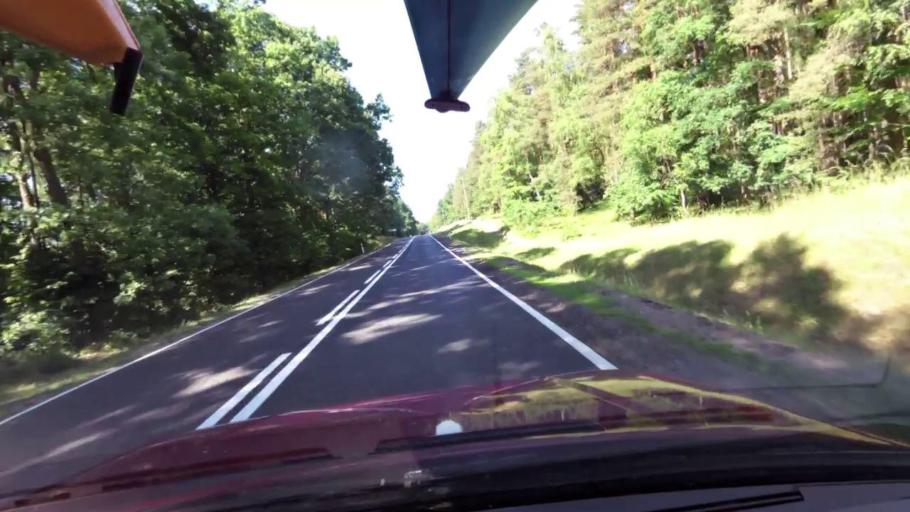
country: PL
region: Pomeranian Voivodeship
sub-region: Powiat bytowski
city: Trzebielino
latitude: 54.1216
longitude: 17.0039
